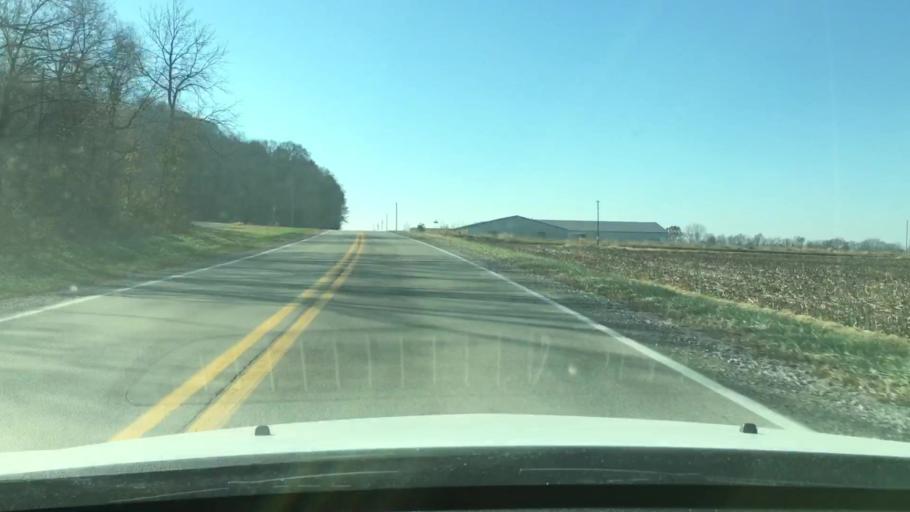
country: US
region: Illinois
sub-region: Morgan County
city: Meredosia
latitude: 39.7331
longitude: -90.5628
